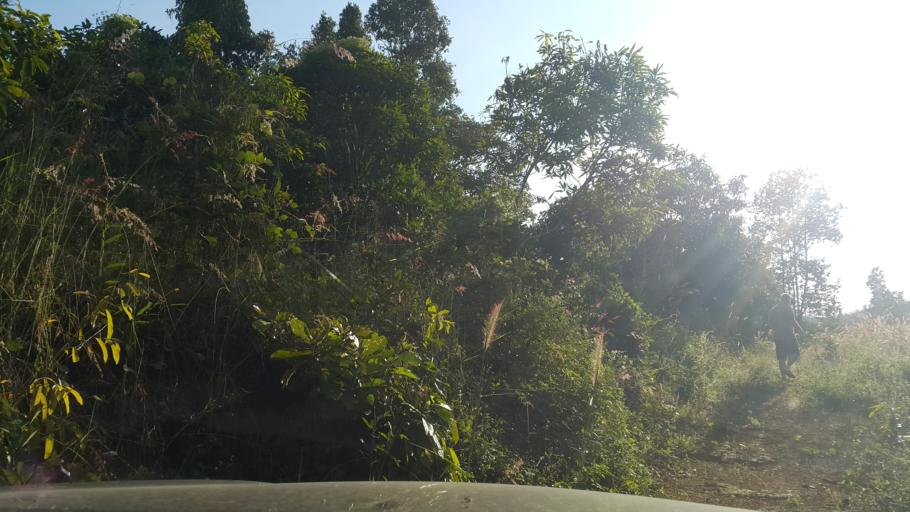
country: TH
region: Chiang Mai
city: San Kamphaeng
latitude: 18.7071
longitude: 99.1962
